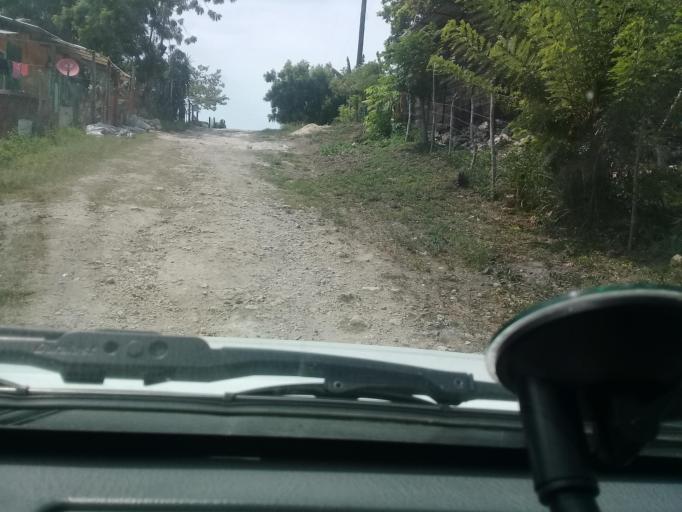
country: MX
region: Veracruz
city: Anahuac
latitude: 22.2135
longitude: -97.8335
